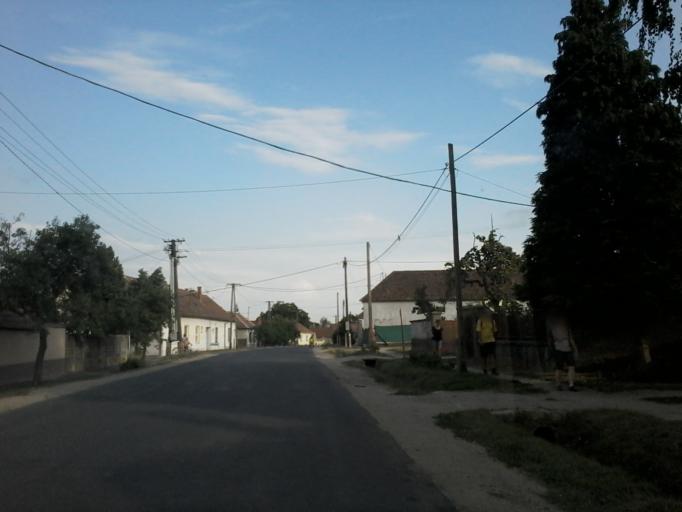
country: HU
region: Vas
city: Sarvar
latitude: 47.2150
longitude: 17.0170
